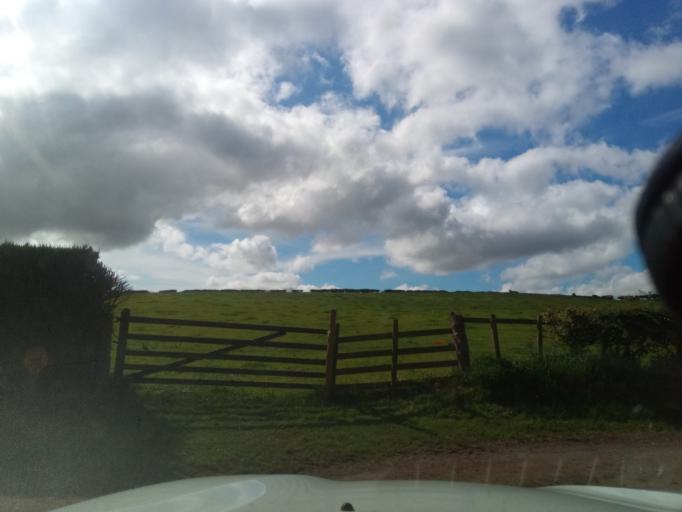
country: GB
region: Scotland
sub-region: The Scottish Borders
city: Saint Boswells
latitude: 55.6030
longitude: -2.6038
